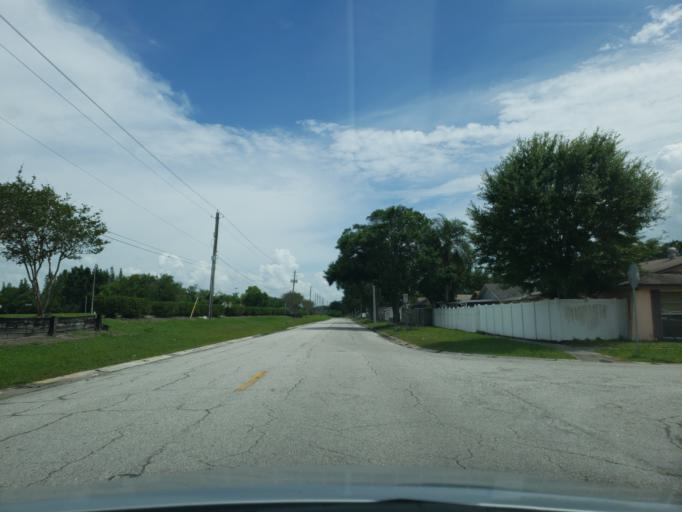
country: US
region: Florida
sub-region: Hillsborough County
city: Town 'n' Country
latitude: 28.0310
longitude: -82.5500
